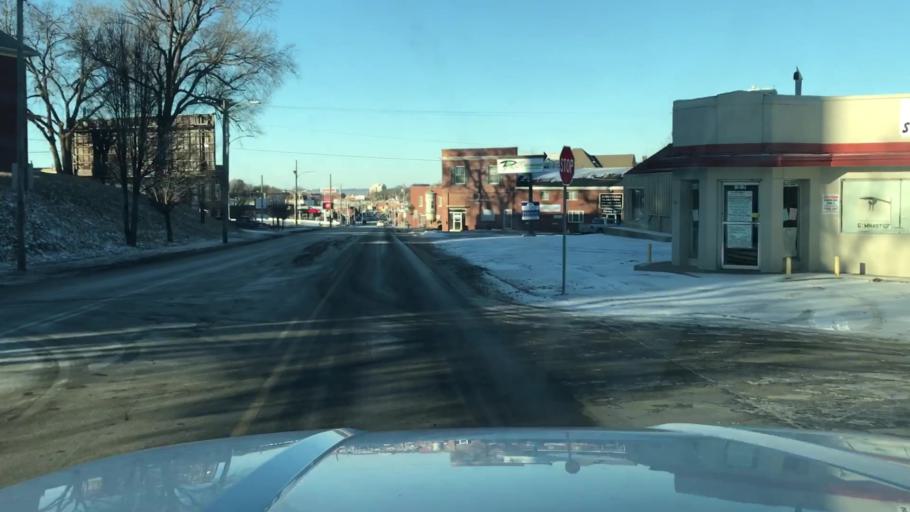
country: US
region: Missouri
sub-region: Buchanan County
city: Saint Joseph
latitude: 39.7764
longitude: -94.8317
